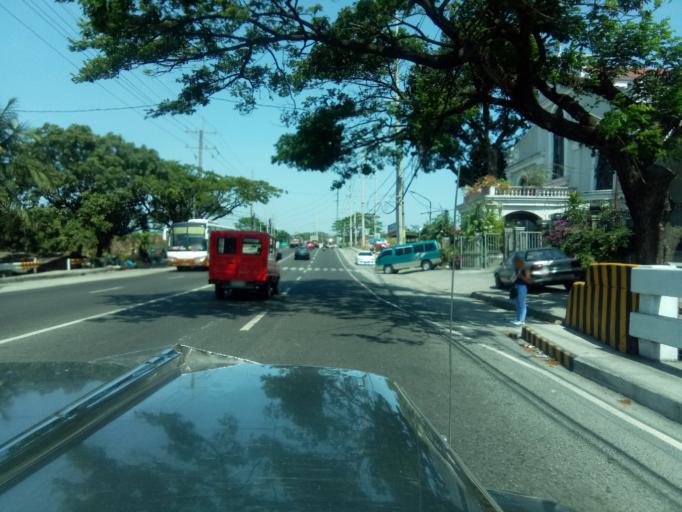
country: PH
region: Calabarzon
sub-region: Province of Cavite
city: Dasmarinas
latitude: 14.2939
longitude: 120.9395
